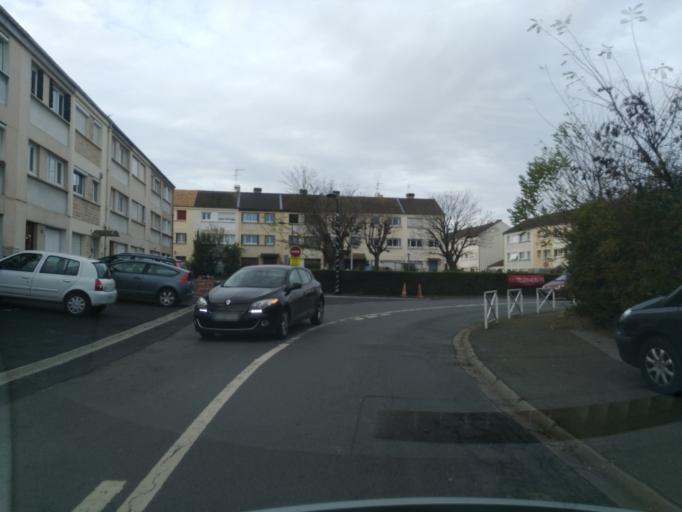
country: FR
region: Ile-de-France
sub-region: Departement des Yvelines
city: Villepreux
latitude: 48.8239
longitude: 1.9998
